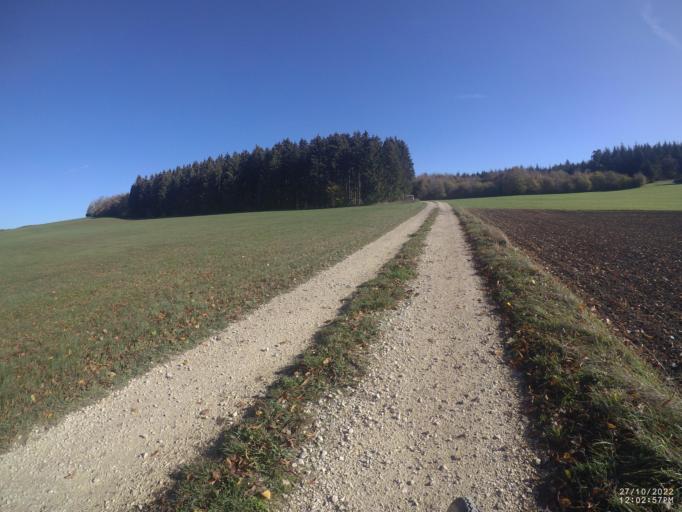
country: DE
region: Baden-Wuerttemberg
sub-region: Regierungsbezirk Stuttgart
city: Bad Ditzenbach
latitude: 48.5578
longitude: 9.7158
